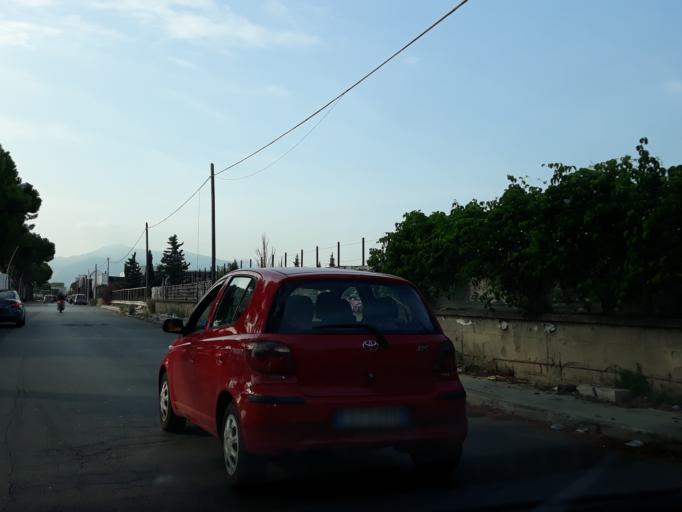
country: IT
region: Sicily
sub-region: Palermo
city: Villa Ciambra
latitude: 38.0881
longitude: 13.3475
